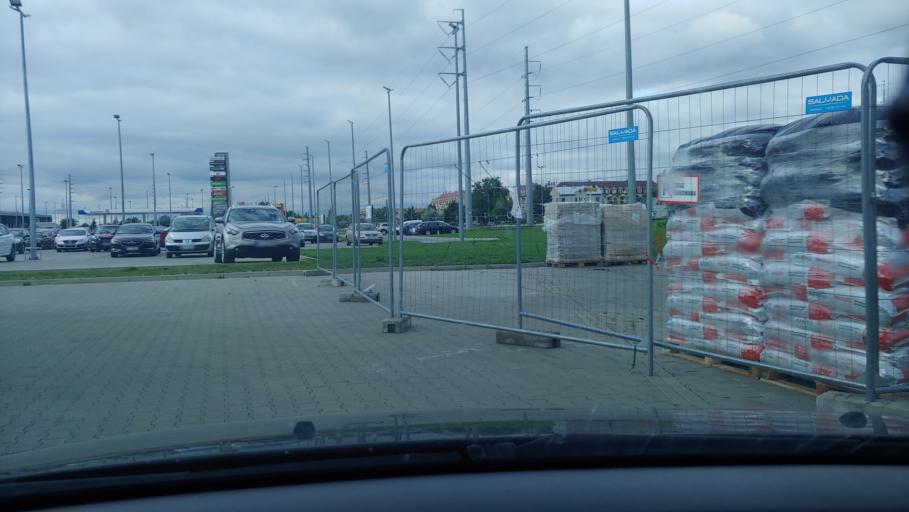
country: PL
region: Subcarpathian Voivodeship
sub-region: Powiat mielecki
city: Mielec
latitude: 50.2861
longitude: 21.4611
